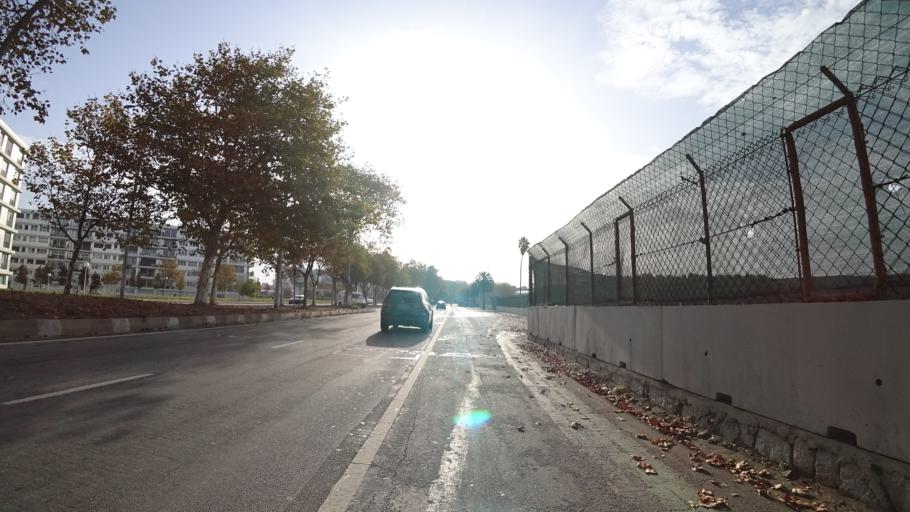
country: PT
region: Porto
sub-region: Matosinhos
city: Matosinhos
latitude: 41.1731
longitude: -8.6829
